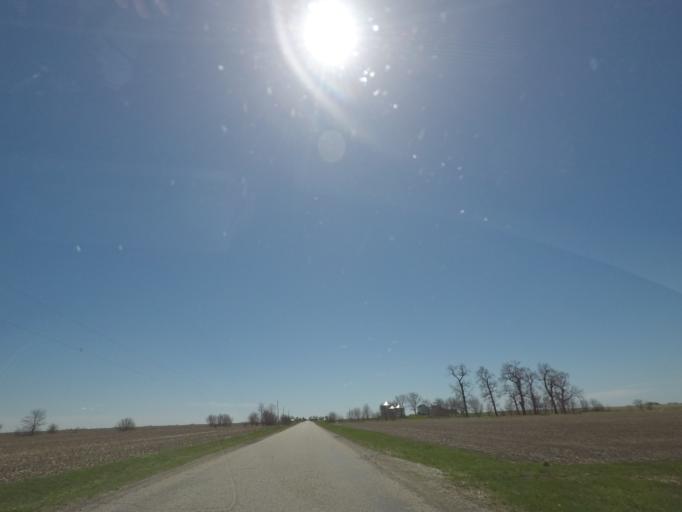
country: US
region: Illinois
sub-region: Logan County
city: Atlanta
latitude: 40.1973
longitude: -89.1942
